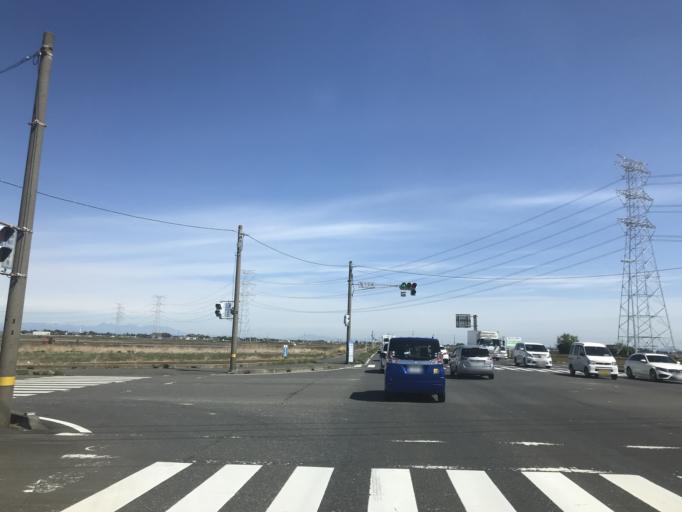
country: JP
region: Ibaraki
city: Ishige
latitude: 36.1217
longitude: 139.9825
